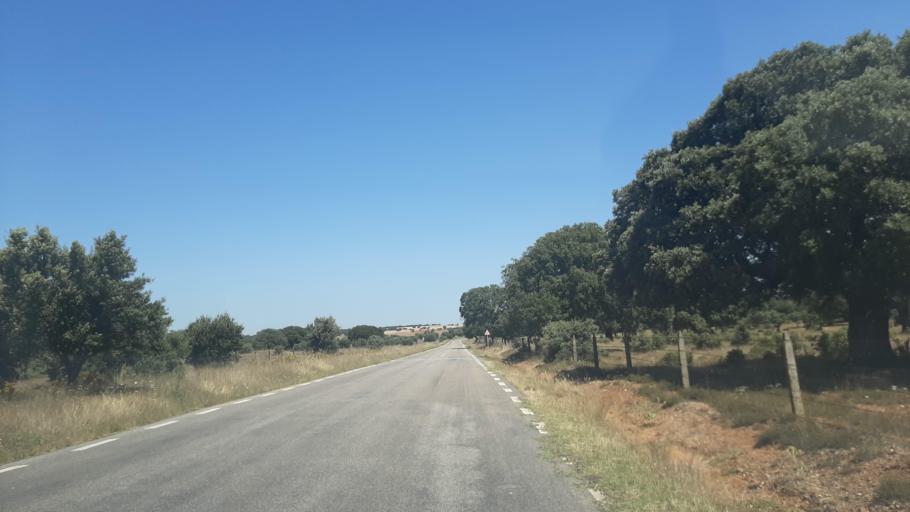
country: ES
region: Castille and Leon
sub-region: Provincia de Salamanca
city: Cabrillas
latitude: 40.7279
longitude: -6.1764
